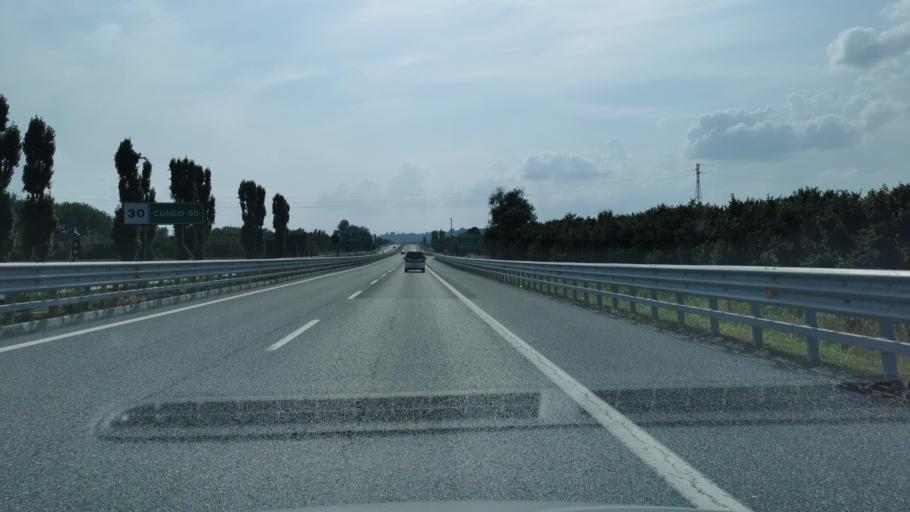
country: IT
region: Piedmont
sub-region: Provincia di Cuneo
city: Cherasco
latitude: 44.6638
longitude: 7.8636
